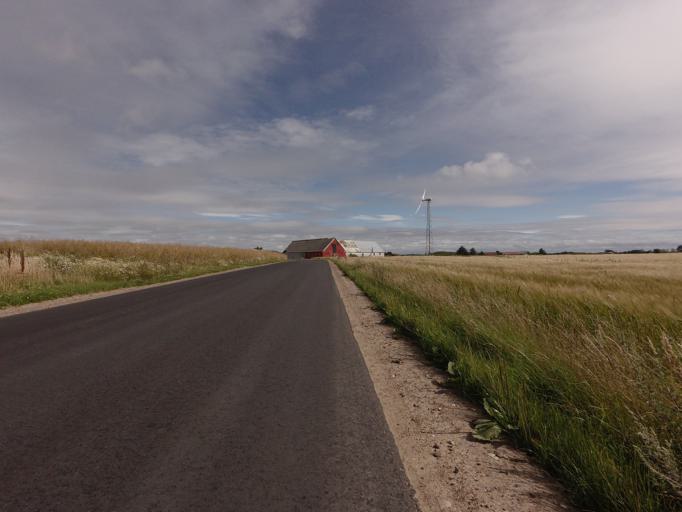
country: DK
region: North Denmark
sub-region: Hjorring Kommune
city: Vra
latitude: 57.3962
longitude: 9.7664
